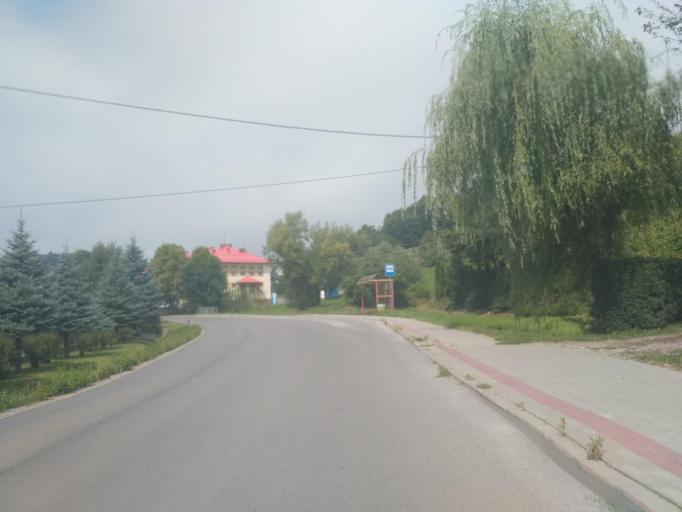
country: PL
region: Subcarpathian Voivodeship
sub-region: Powiat rzeszowski
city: Chmielnik
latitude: 49.9918
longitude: 22.1086
